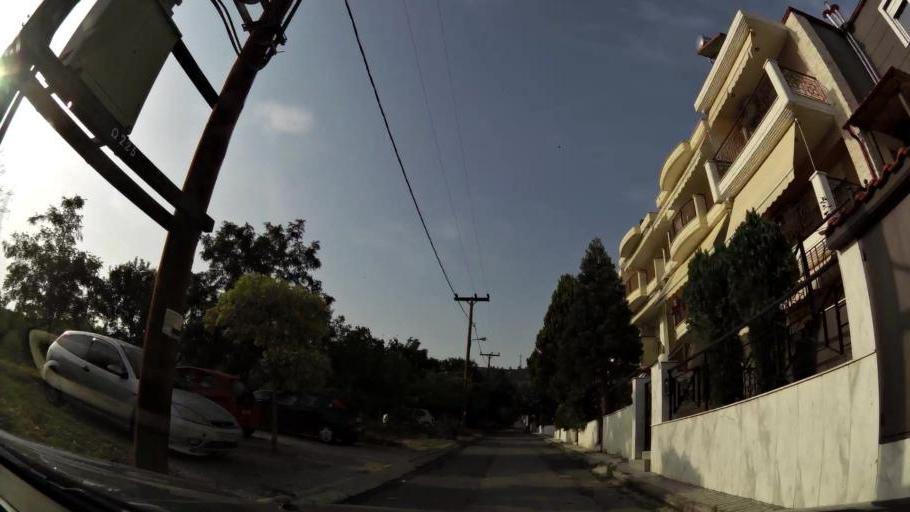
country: GR
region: Central Macedonia
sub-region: Nomos Thessalonikis
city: Oraiokastro
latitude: 40.7222
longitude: 22.9017
